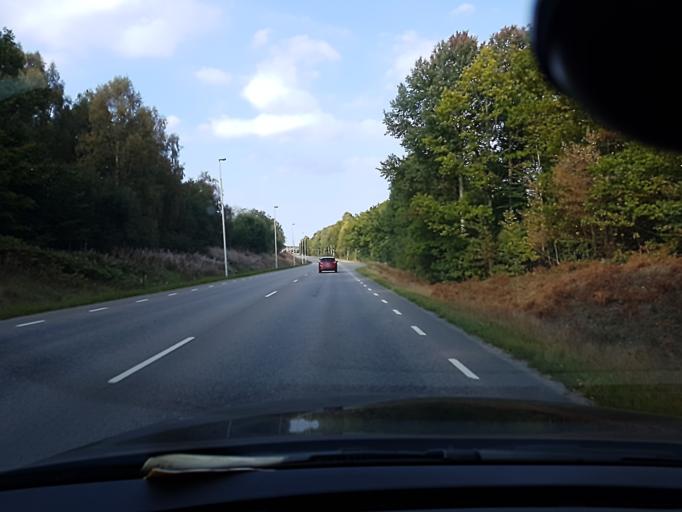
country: SE
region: Kronoberg
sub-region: Vaxjo Kommun
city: Vaexjoe
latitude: 56.8684
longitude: 14.7885
